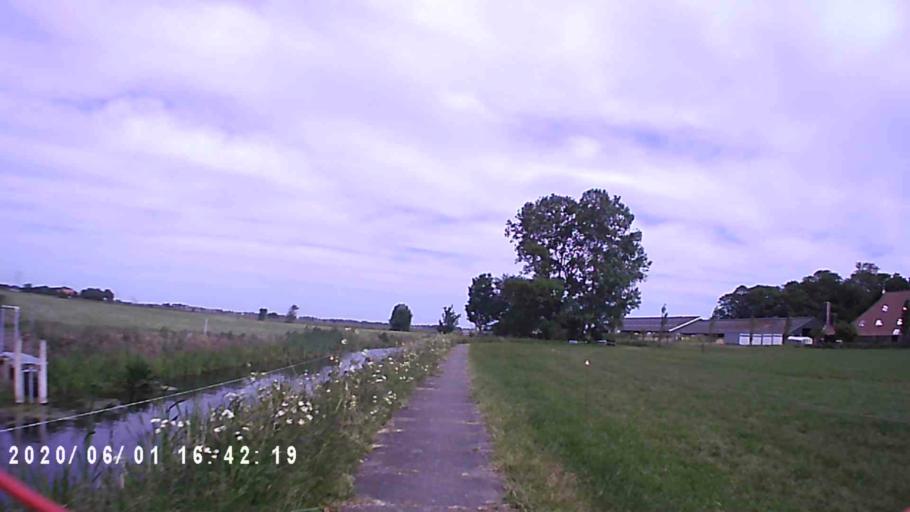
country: NL
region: Friesland
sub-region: Gemeente Boarnsterhim
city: Warten
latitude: 53.1830
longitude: 5.8794
